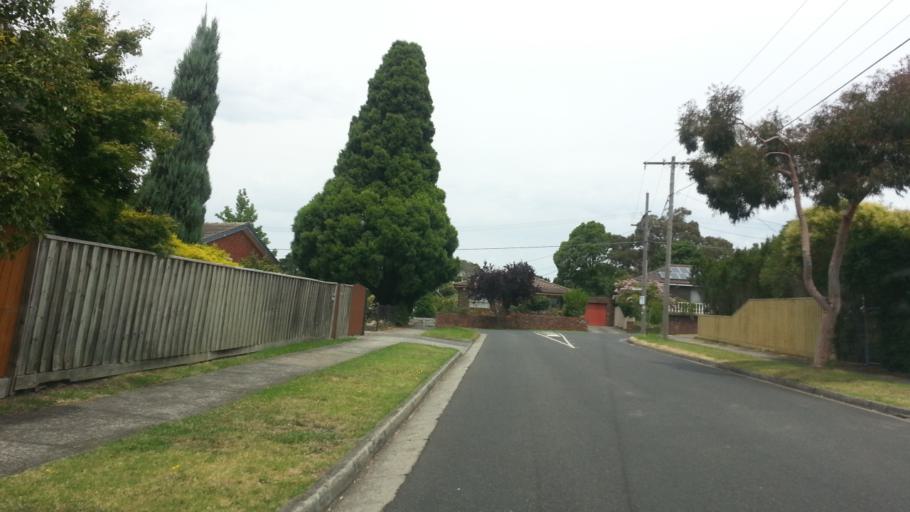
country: AU
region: Victoria
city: Mitcham
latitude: -37.8265
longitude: 145.2020
